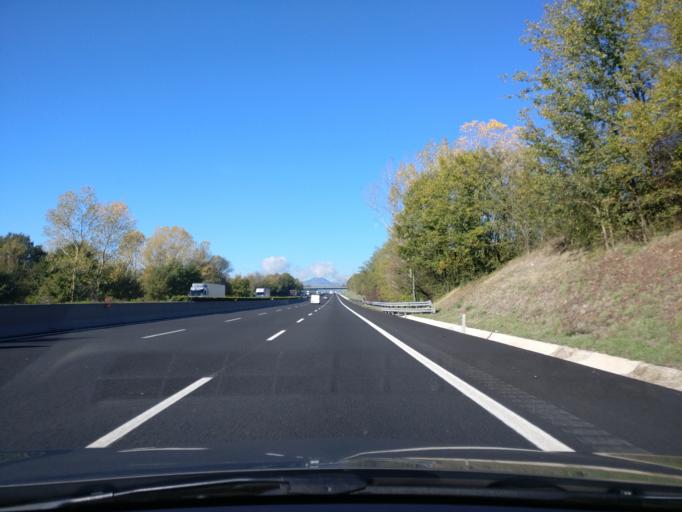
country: IT
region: Latium
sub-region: Provincia di Frosinone
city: Pofi
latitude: 41.5519
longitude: 13.4478
